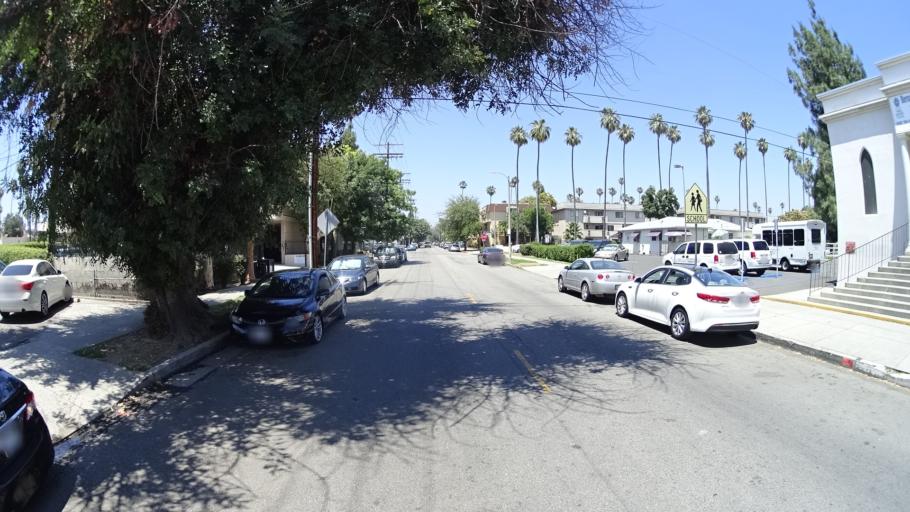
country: US
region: California
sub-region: Los Angeles County
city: Van Nuys
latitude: 34.1891
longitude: -118.4466
